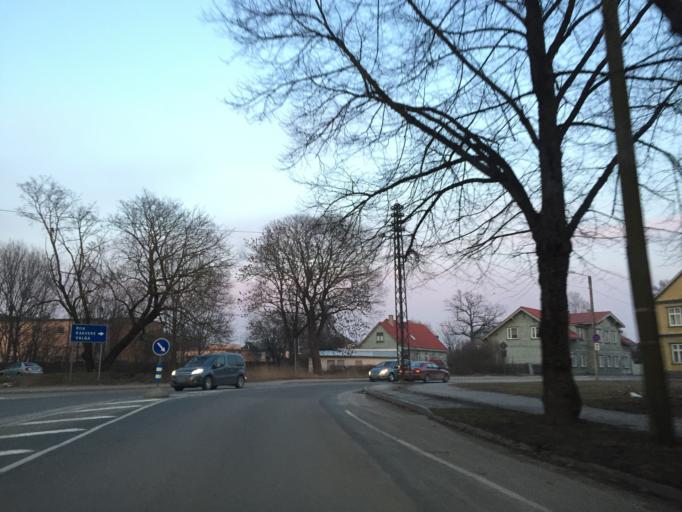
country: EE
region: Paernumaa
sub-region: Paernu linn
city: Parnu
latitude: 58.3860
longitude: 24.5112
